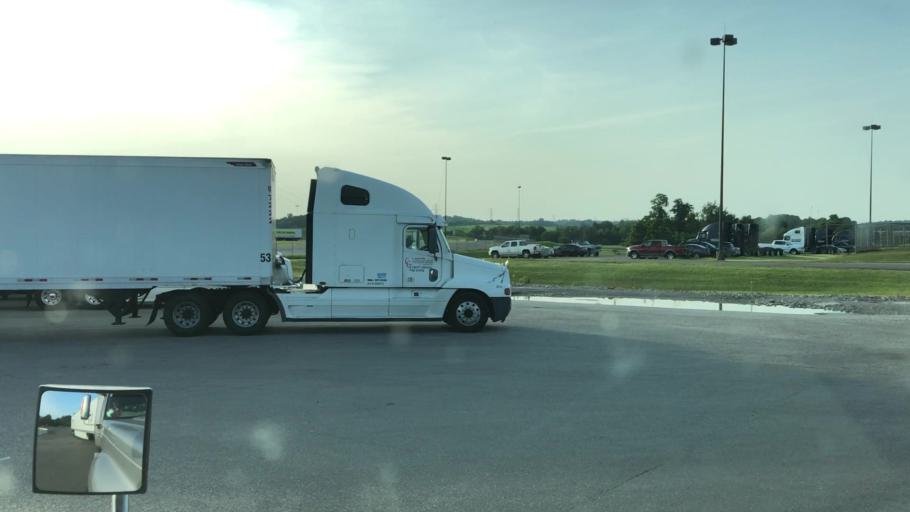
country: US
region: Ohio
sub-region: Muskingum County
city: Pleasant Grove
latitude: 39.9845
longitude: -81.9476
